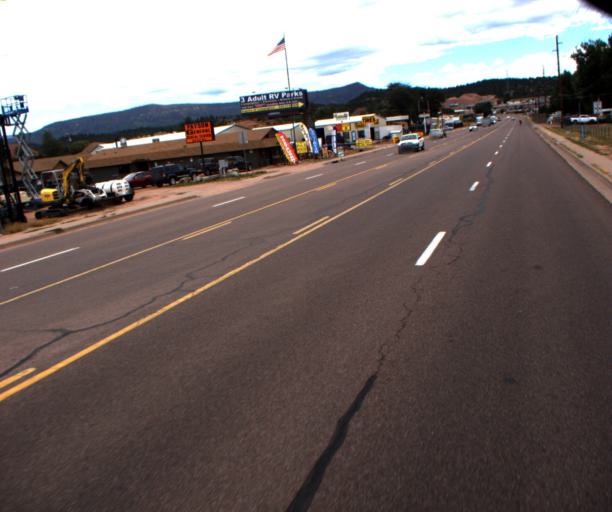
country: US
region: Arizona
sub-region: Gila County
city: Sun Valley
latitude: 34.2539
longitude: -111.2626
